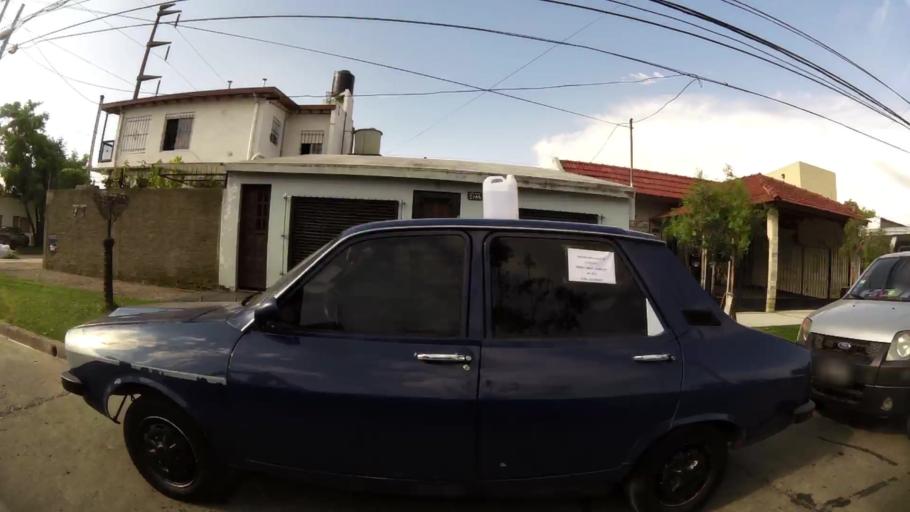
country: AR
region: Buenos Aires
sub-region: Partido de Merlo
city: Merlo
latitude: -34.6606
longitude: -58.7342
